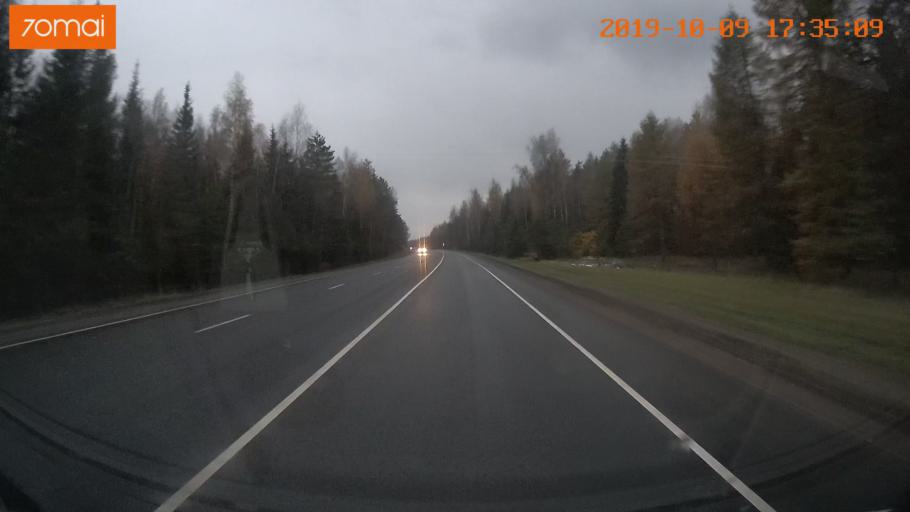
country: RU
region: Ivanovo
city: Bogorodskoye
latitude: 57.0979
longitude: 41.0043
